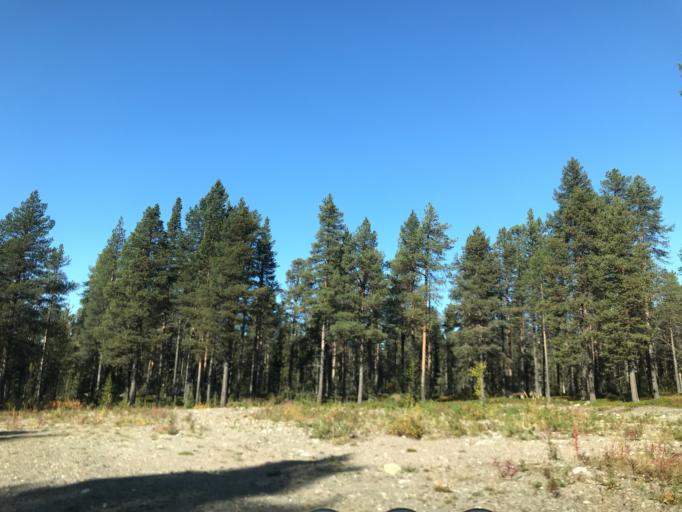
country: SE
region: Norrbotten
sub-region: Gallivare Kommun
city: Malmberget
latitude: 67.6498
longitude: 21.0816
